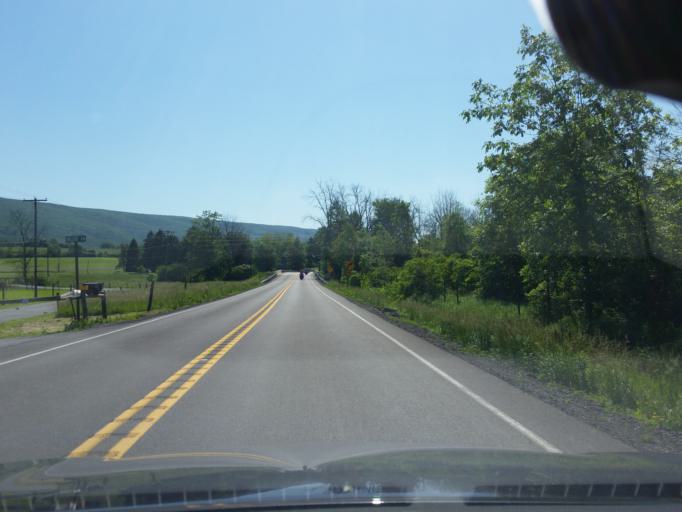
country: US
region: Pennsylvania
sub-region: Northumberland County
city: Dewart
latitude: 41.1156
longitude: -76.9405
